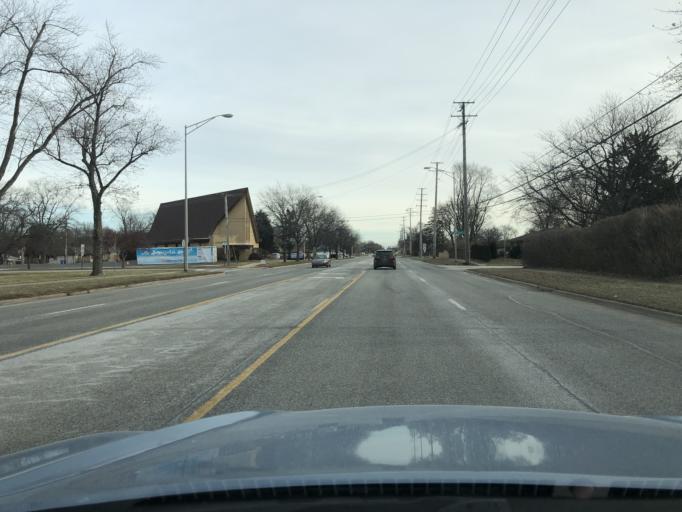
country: US
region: Illinois
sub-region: Cook County
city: Mount Prospect
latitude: 42.0661
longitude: -87.9140
